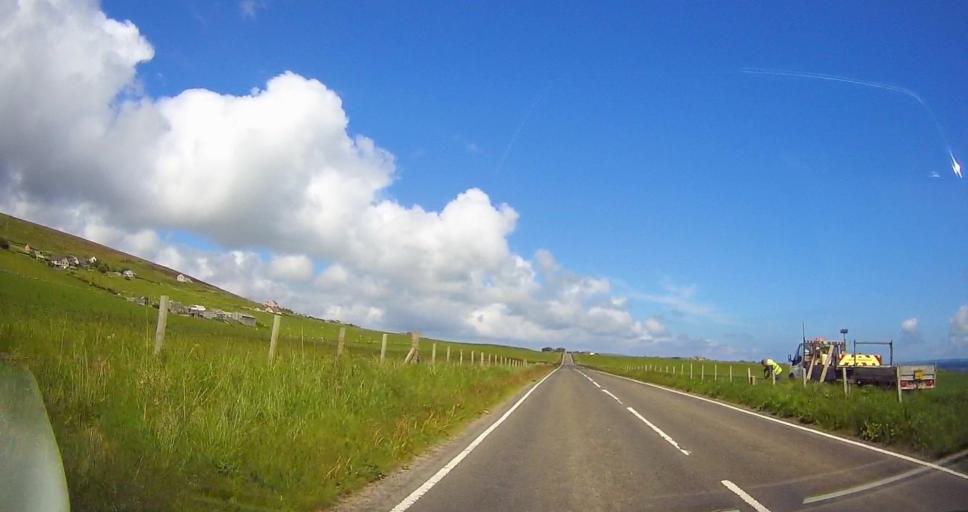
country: GB
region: Scotland
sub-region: Orkney Islands
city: Orkney
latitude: 59.0146
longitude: -3.1080
